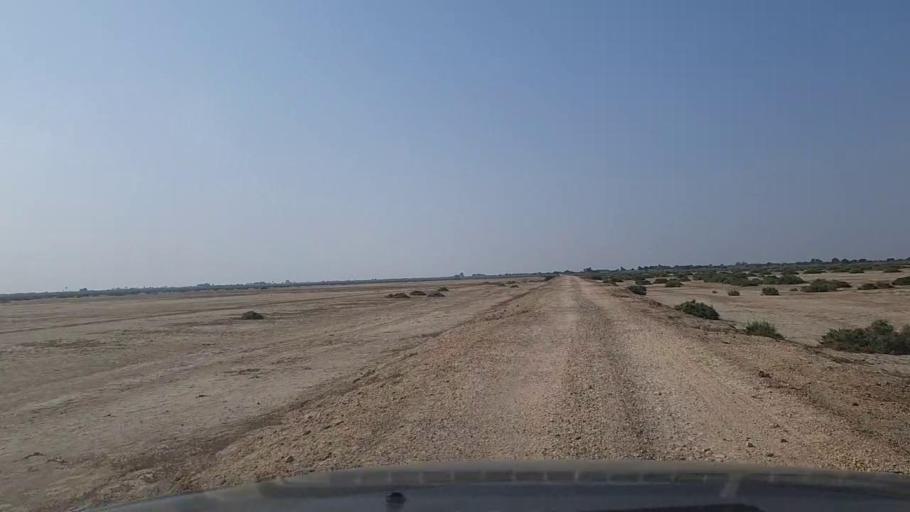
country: PK
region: Sindh
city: Mirpur Sakro
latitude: 24.4322
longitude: 67.7303
